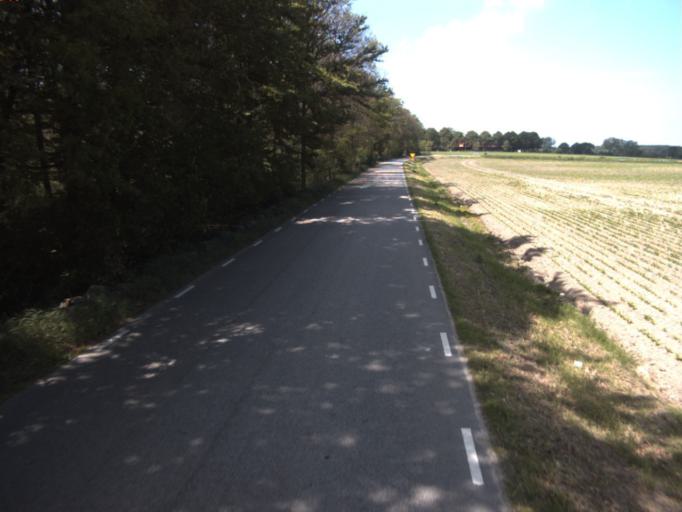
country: SE
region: Skane
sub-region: Helsingborg
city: Barslov
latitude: 56.0403
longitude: 12.8069
